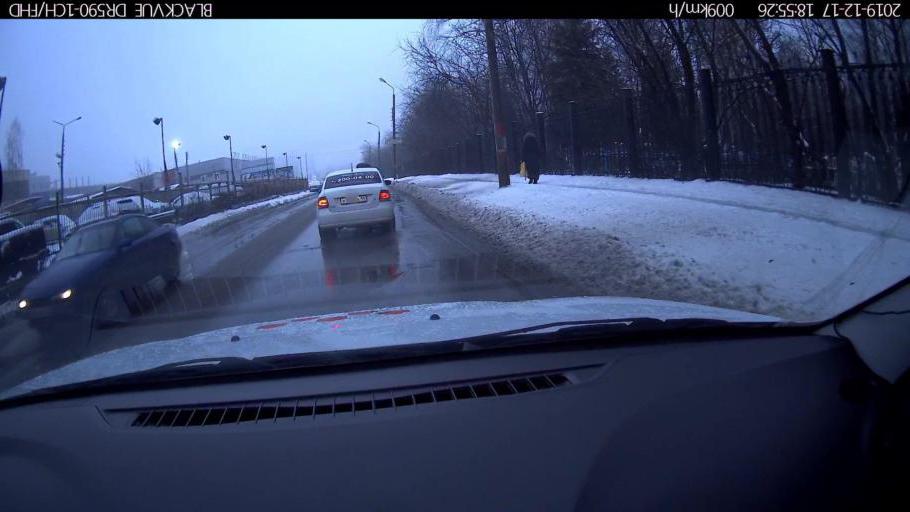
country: RU
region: Nizjnij Novgorod
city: Nizhniy Novgorod
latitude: 56.2837
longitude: 43.9986
